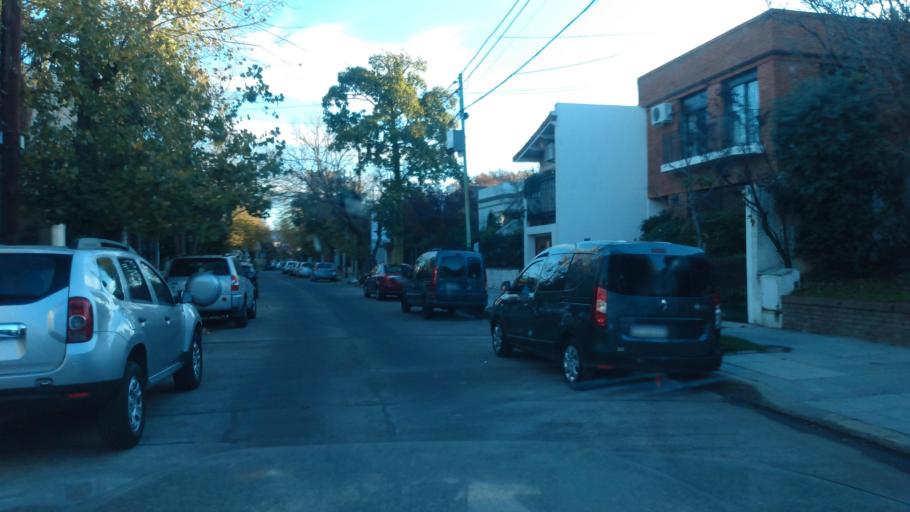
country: AR
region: Buenos Aires F.D.
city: Villa Santa Rita
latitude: -34.5823
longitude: -58.4833
